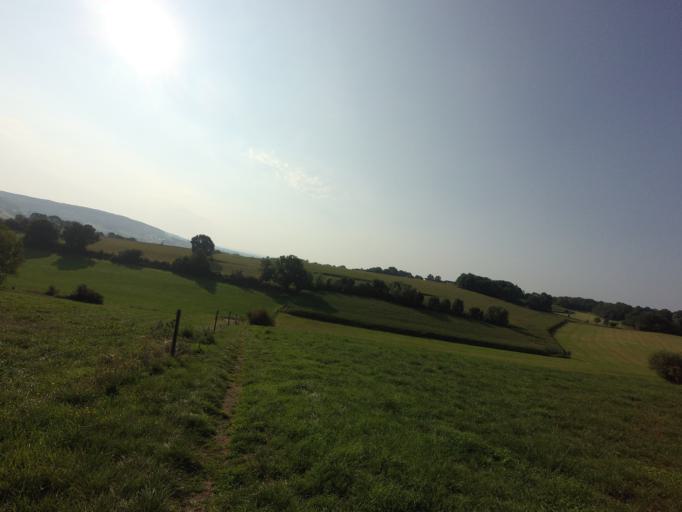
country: BE
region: Wallonia
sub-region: Province de Liege
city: Plombieres
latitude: 50.7805
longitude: 5.9021
